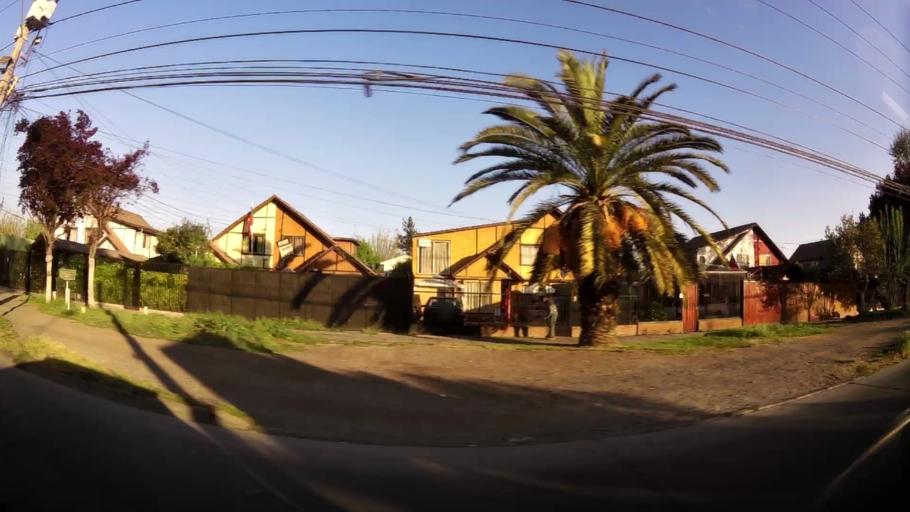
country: CL
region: Santiago Metropolitan
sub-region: Provincia de Santiago
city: Lo Prado
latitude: -33.4688
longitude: -70.7320
